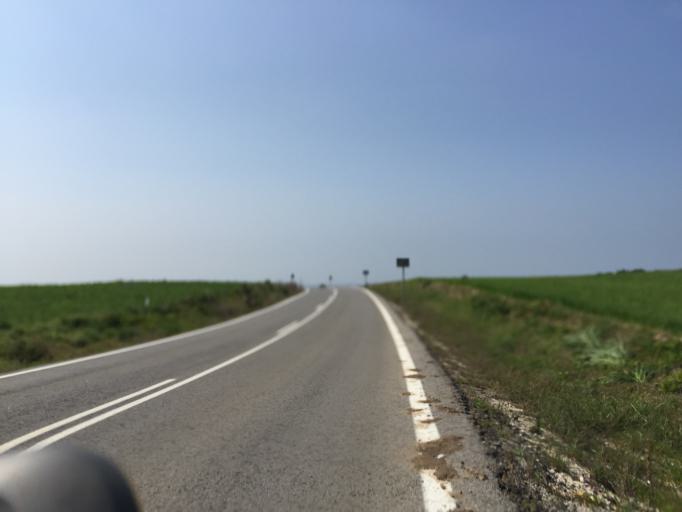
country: ES
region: Andalusia
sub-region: Provincia de Cadiz
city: Vejer de la Frontera
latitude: 36.2298
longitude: -6.0370
